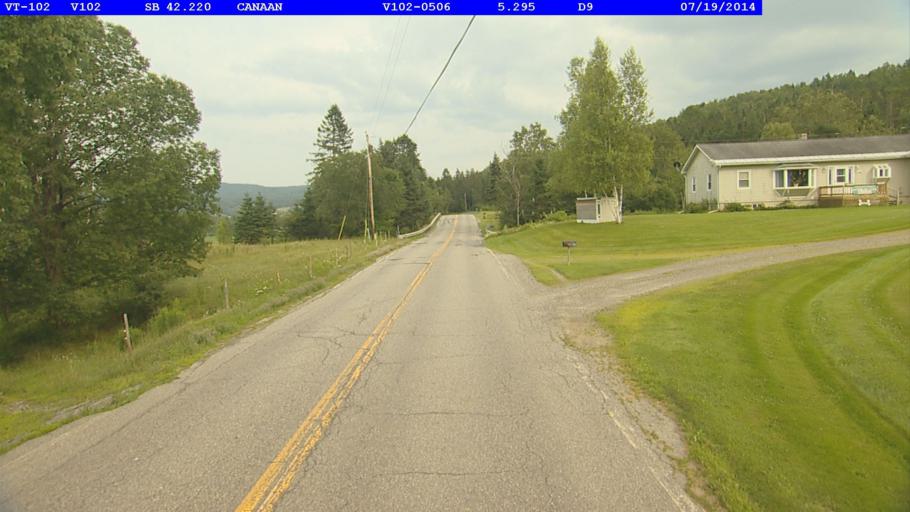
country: US
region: New Hampshire
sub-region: Coos County
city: Colebrook
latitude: 44.9762
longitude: -71.5382
